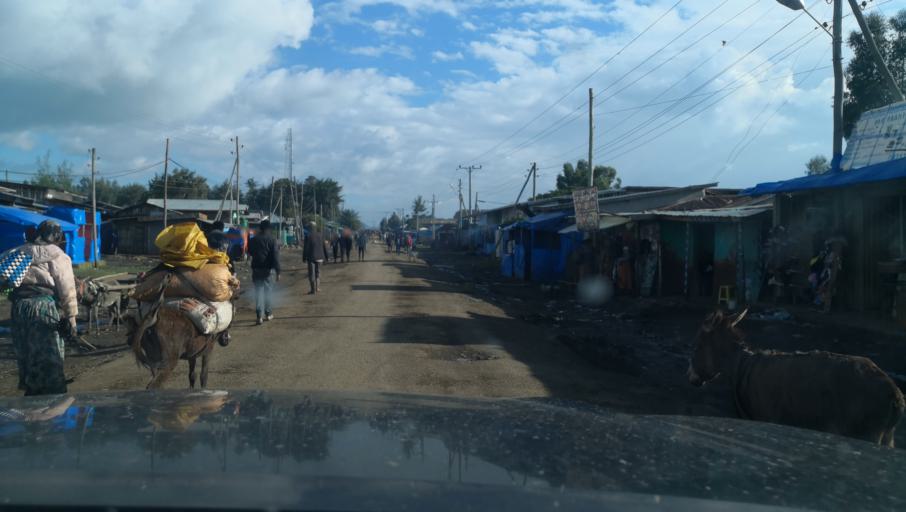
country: ET
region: Oromiya
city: Tulu Bolo
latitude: 8.4661
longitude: 38.2525
